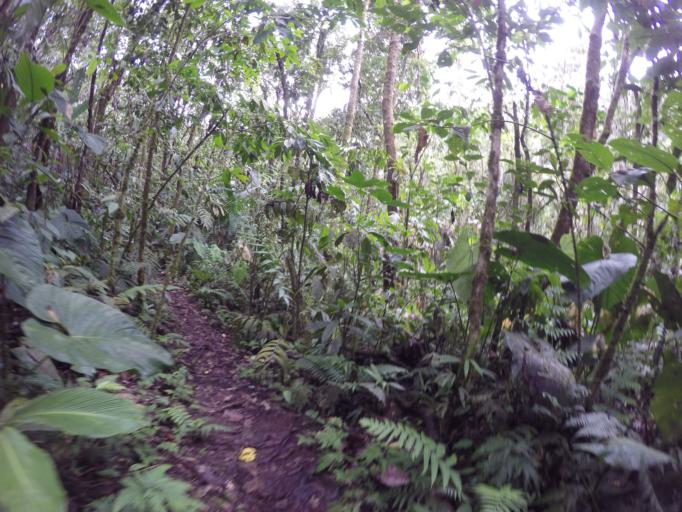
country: CO
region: Quindio
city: Filandia
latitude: 4.7093
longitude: -75.6764
